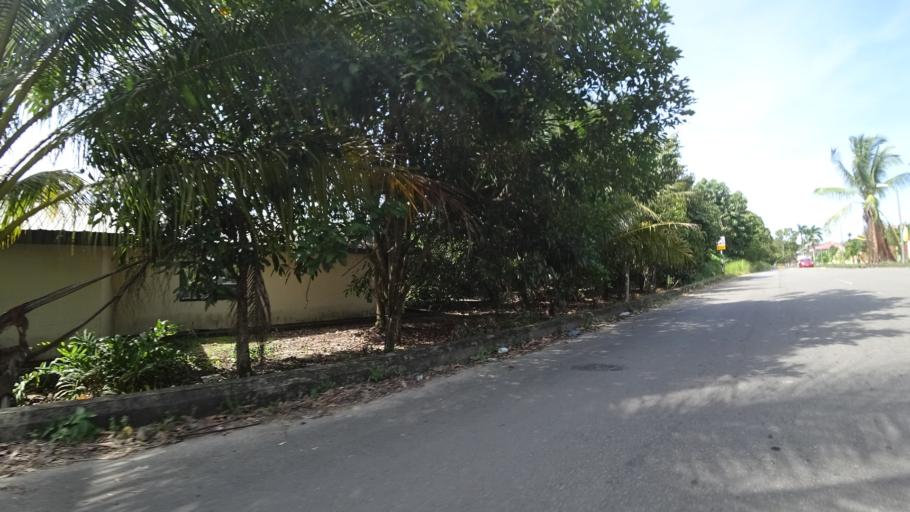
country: BN
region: Brunei and Muara
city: Bandar Seri Begawan
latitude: 4.8712
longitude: 114.8533
